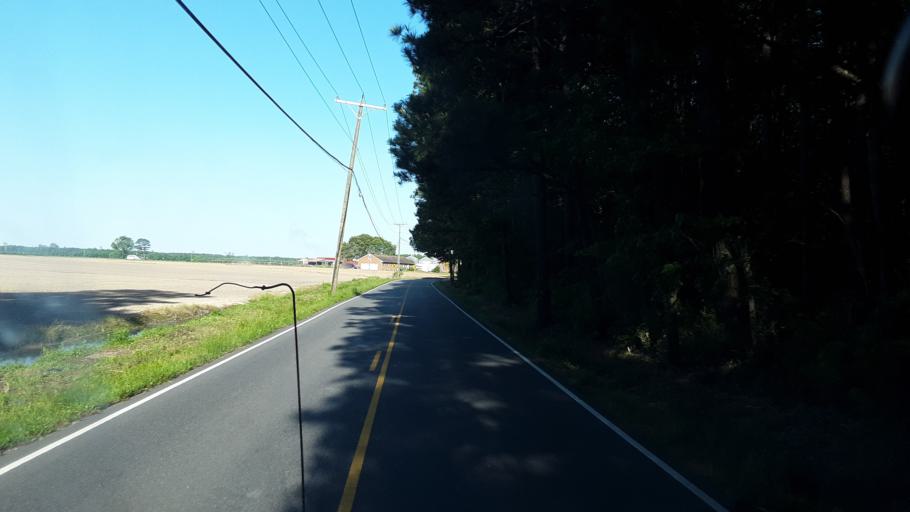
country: US
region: Virginia
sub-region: City of Virginia Beach
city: Virginia Beach
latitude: 36.7203
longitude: -76.0432
